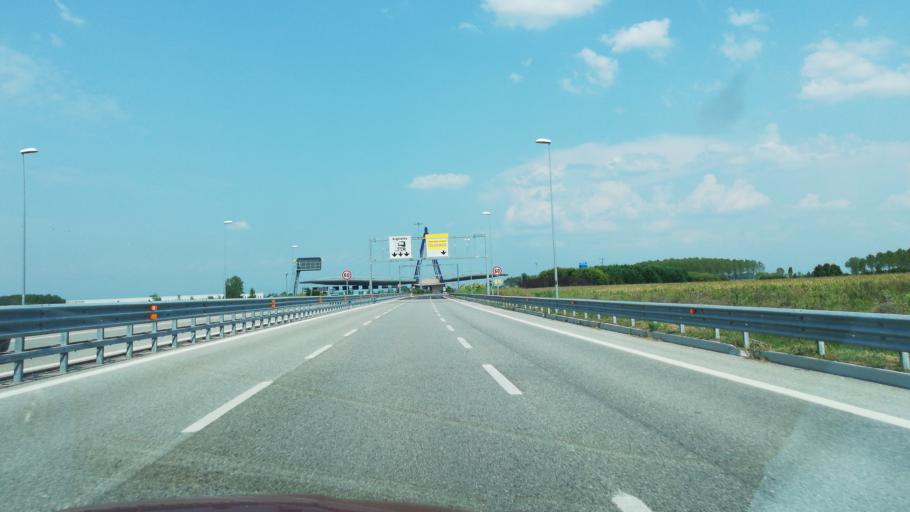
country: IT
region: Friuli Venezia Giulia
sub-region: Provincia di Udine
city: Ronchis
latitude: 45.8028
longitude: 13.0214
